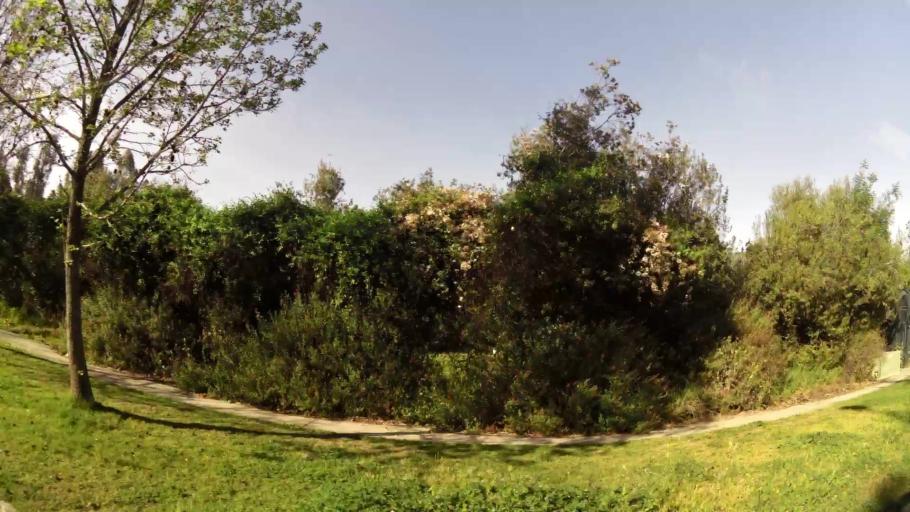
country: CL
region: Santiago Metropolitan
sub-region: Provincia de Santiago
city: Villa Presidente Frei, Nunoa, Santiago, Chile
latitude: -33.4957
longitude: -70.5457
